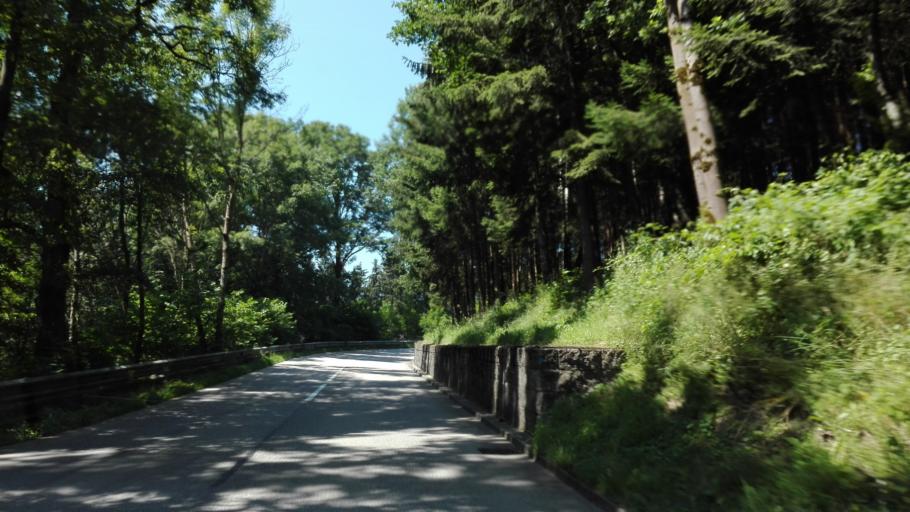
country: AT
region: Upper Austria
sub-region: Politischer Bezirk Grieskirchen
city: Grieskirchen
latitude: 48.3676
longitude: 13.8706
